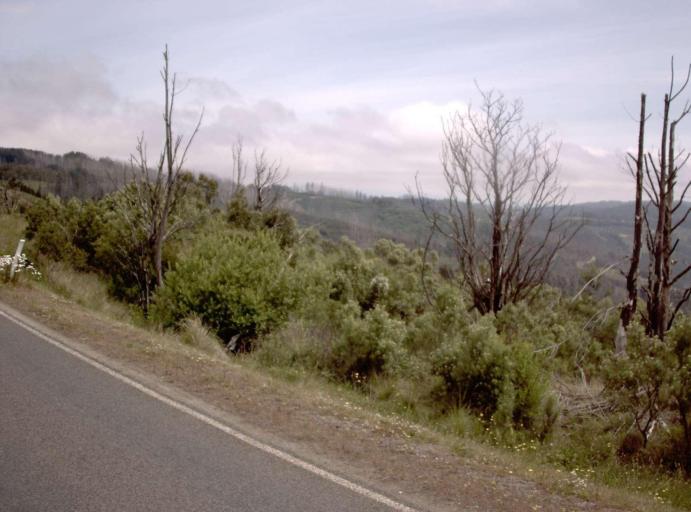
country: AU
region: Victoria
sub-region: Latrobe
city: Traralgon
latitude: -38.4018
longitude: 146.5628
